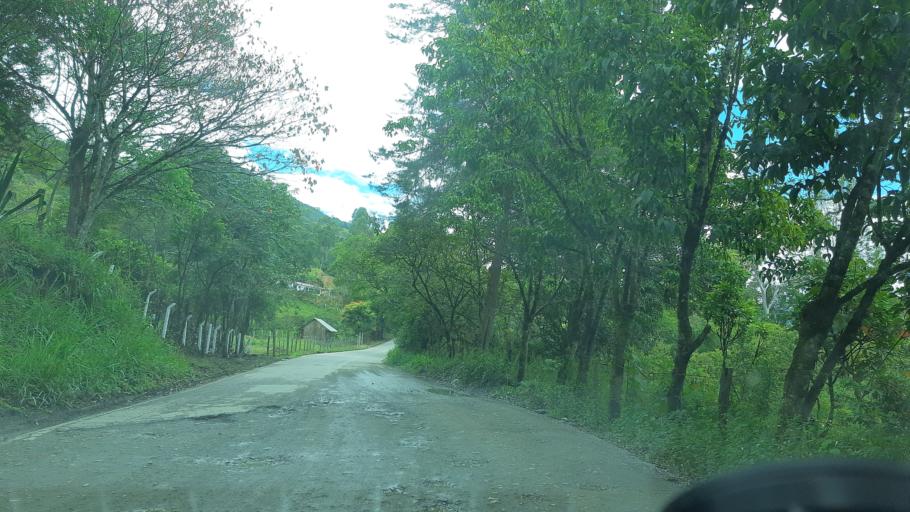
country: CO
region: Boyaca
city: Garagoa
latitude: 5.0631
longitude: -73.3832
